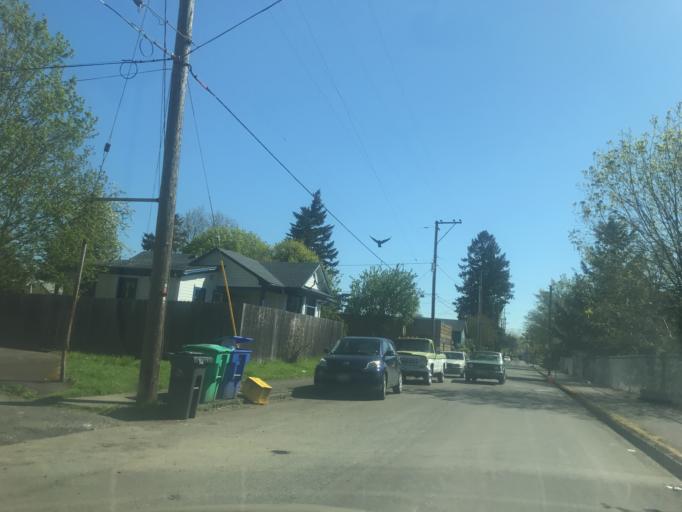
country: US
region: Oregon
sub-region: Multnomah County
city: Lents
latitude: 45.4865
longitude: -122.5976
